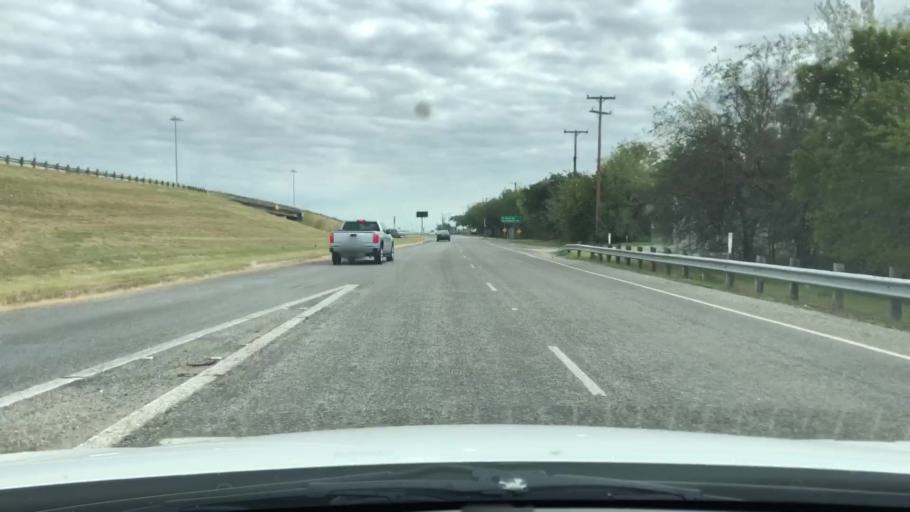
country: US
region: Texas
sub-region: Bexar County
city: Lackland Air Force Base
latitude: 29.4069
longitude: -98.6011
